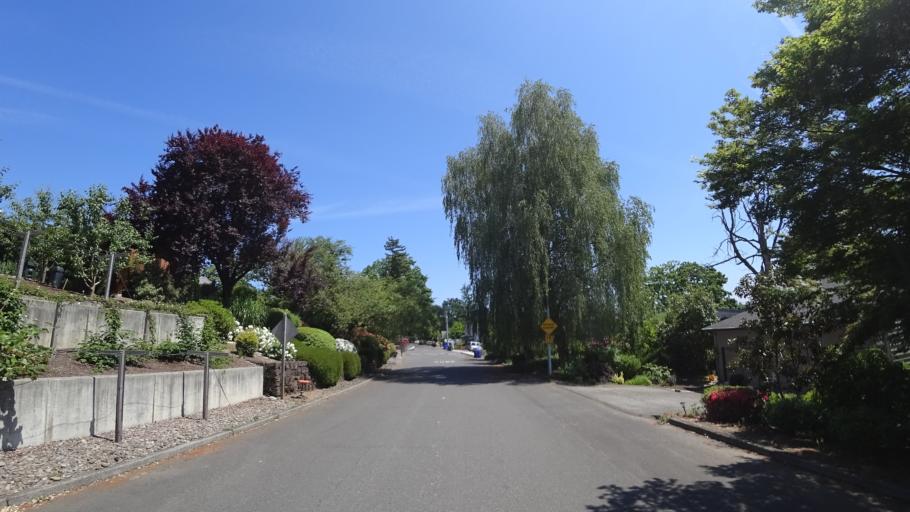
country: US
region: Oregon
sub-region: Multnomah County
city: Fairview
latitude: 45.5520
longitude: -122.4510
